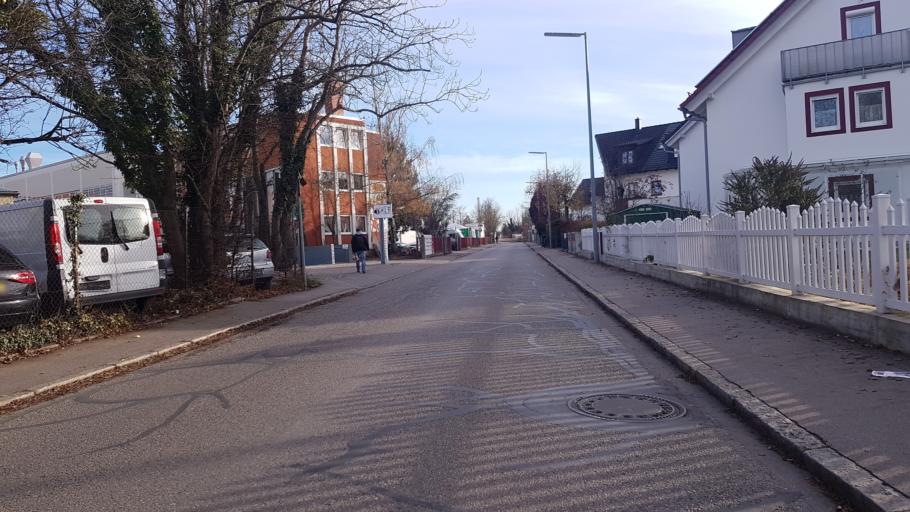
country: DE
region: Bavaria
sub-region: Upper Bavaria
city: Oberschleissheim
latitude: 48.2103
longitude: 11.5391
